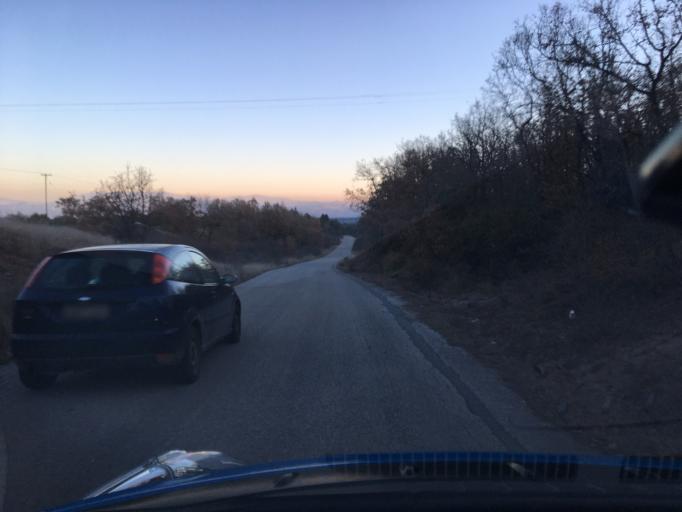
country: GR
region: West Macedonia
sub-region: Nomos Kozanis
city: Kozani
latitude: 40.2646
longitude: 21.7469
